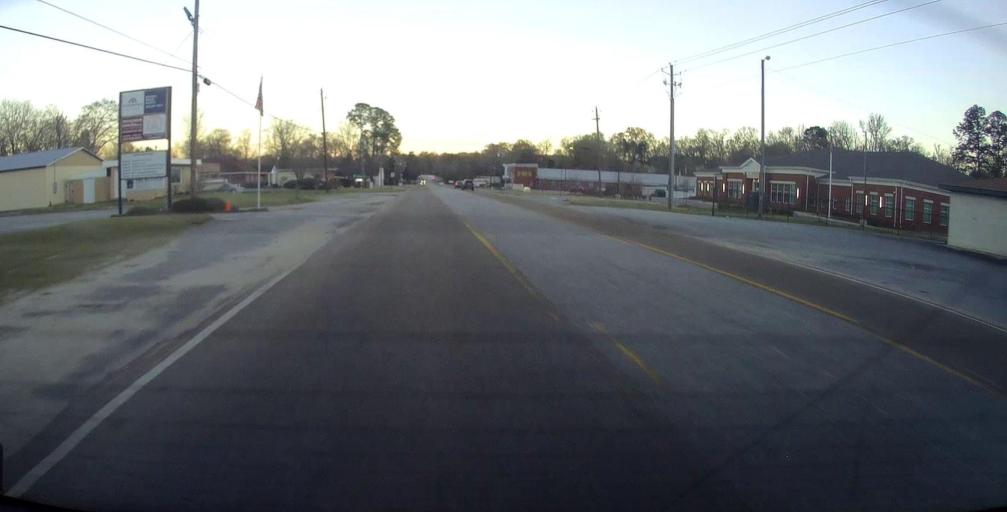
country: US
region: Alabama
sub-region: Russell County
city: Phenix City
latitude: 32.4793
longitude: -85.0273
